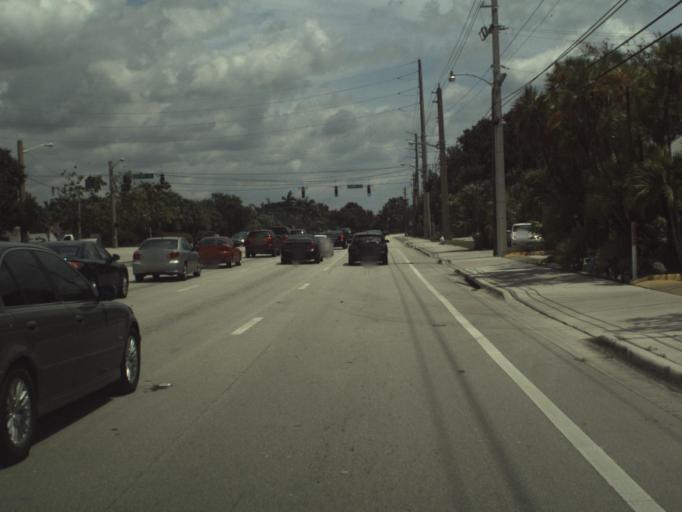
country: US
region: Florida
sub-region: Palm Beach County
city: Jupiter
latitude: 26.9405
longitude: -80.0932
